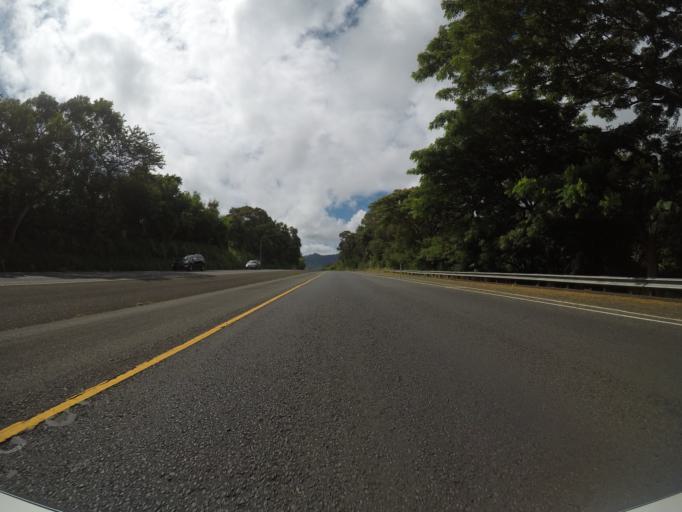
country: US
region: Hawaii
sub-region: Honolulu County
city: Waimanalo
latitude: 21.3608
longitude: -157.7354
